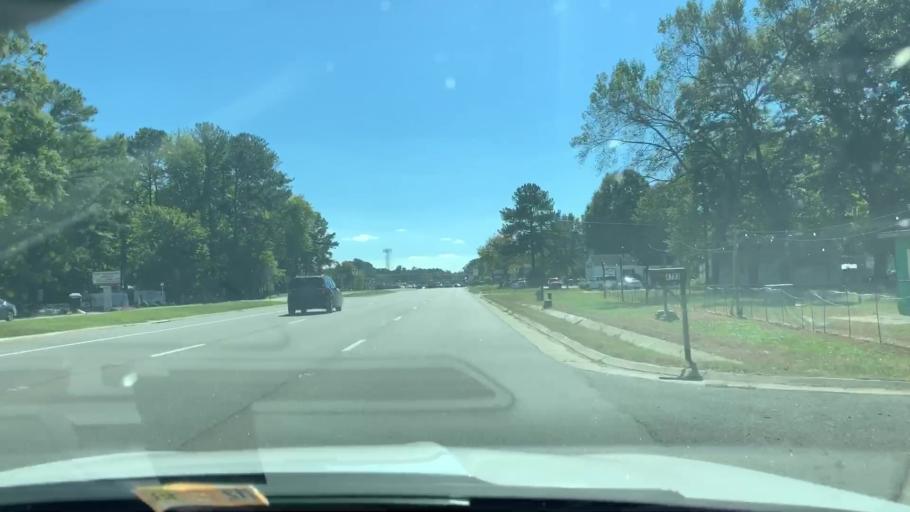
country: US
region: Virginia
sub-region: York County
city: Yorktown
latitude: 37.1506
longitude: -76.4602
